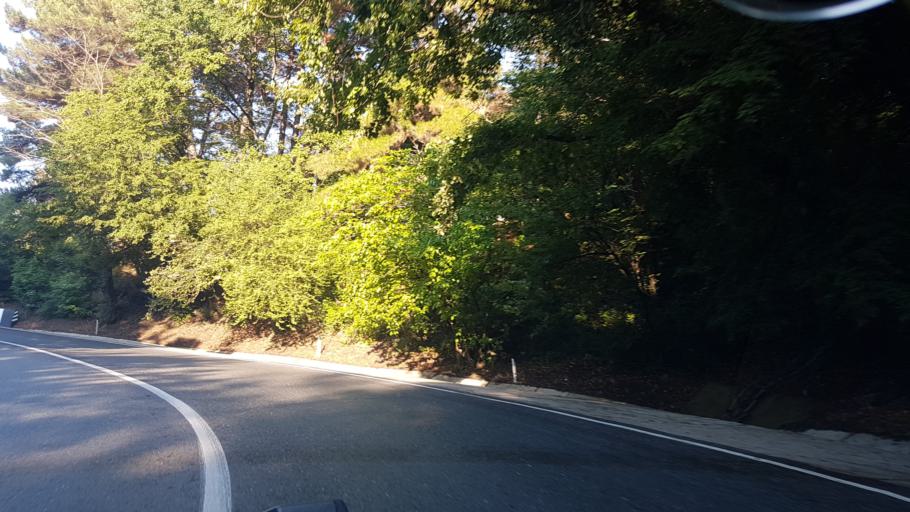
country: RU
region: Krasnodarskiy
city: Gornoye Loo
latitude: 43.6680
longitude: 39.6158
